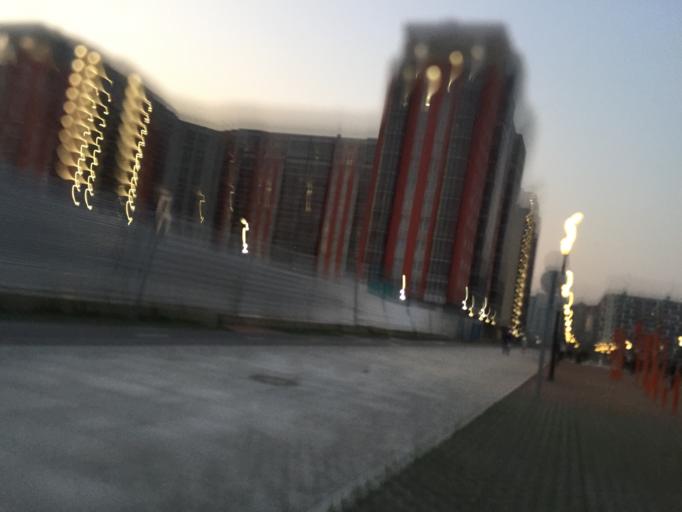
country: RU
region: Leningrad
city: Bugry
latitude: 60.0602
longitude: 30.3980
